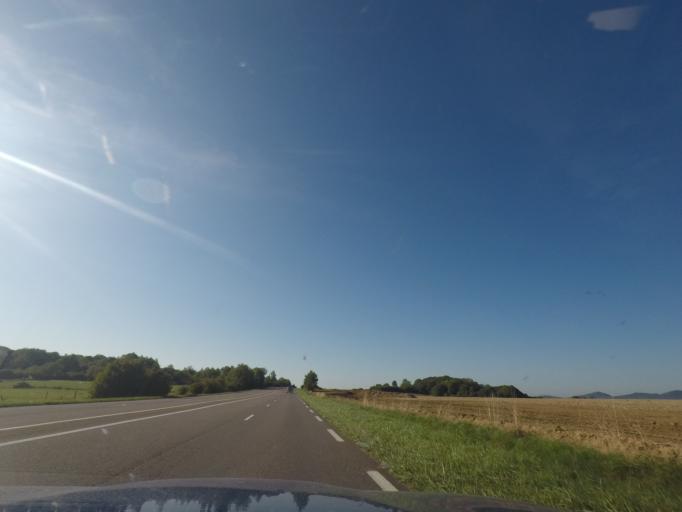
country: FR
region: Lorraine
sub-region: Departement de la Moselle
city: Hettange-Grande
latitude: 49.4333
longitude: 6.1663
